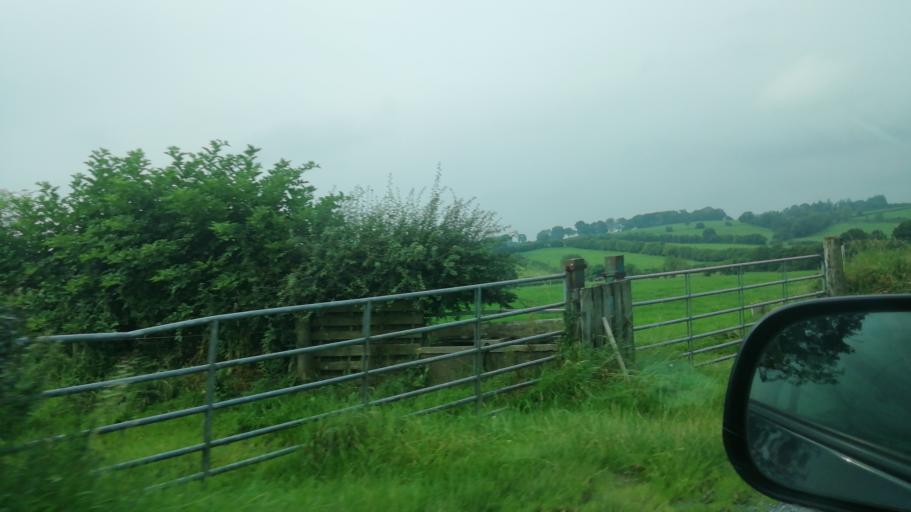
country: IE
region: Munster
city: Fethard
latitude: 52.5786
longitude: -7.6322
